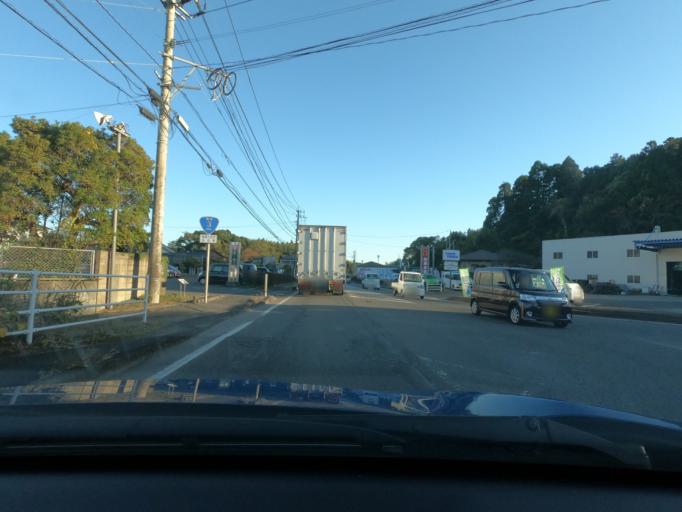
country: JP
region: Kagoshima
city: Satsumasendai
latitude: 31.8421
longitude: 130.2811
